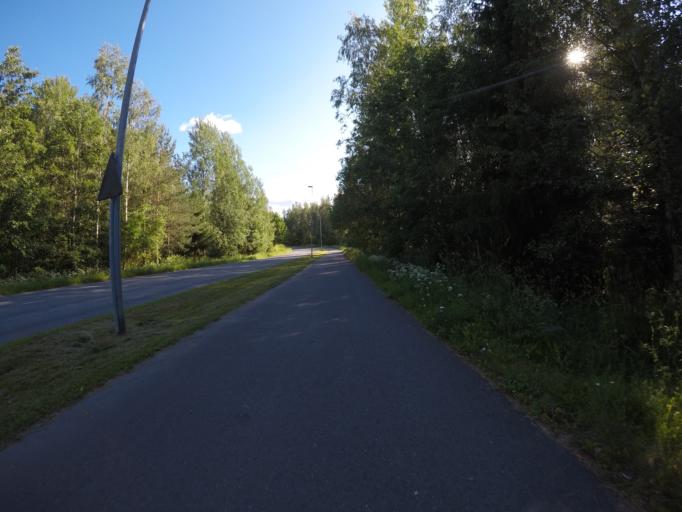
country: FI
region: Haeme
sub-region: Haemeenlinna
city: Haemeenlinna
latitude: 61.0168
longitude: 24.4993
